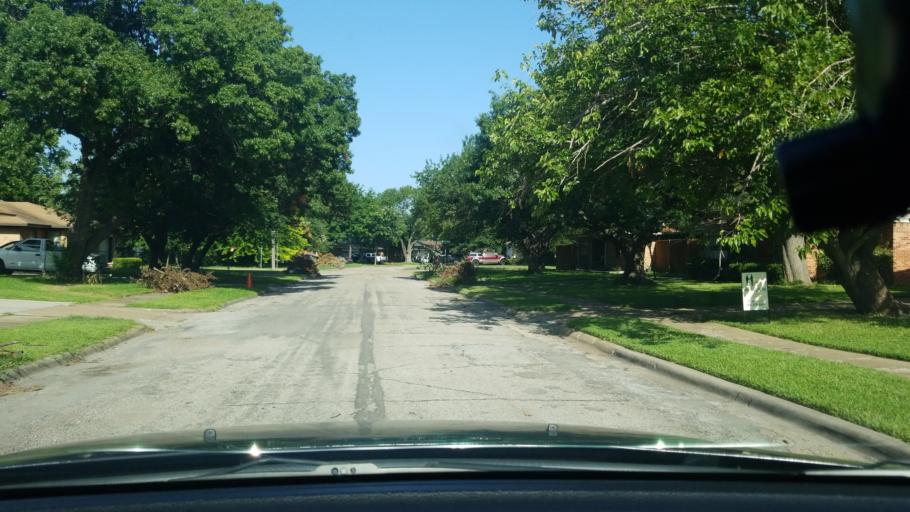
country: US
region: Texas
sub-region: Dallas County
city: Mesquite
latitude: 32.8116
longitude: -96.6761
